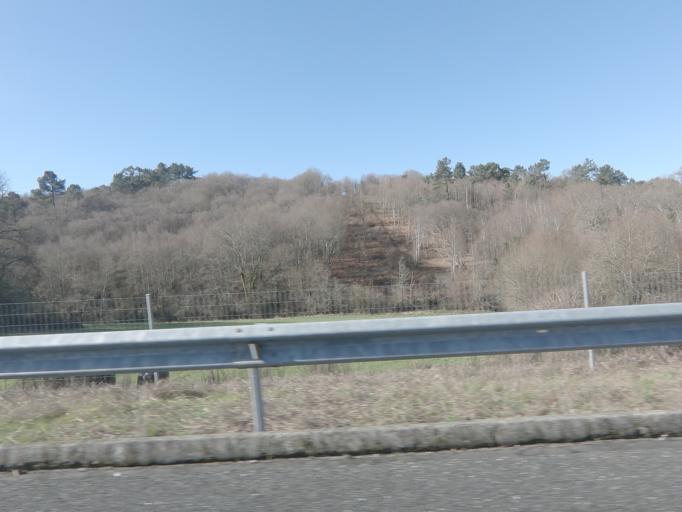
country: ES
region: Galicia
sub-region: Provincia de Pontevedra
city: Lalin
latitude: 42.6671
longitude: -8.1481
